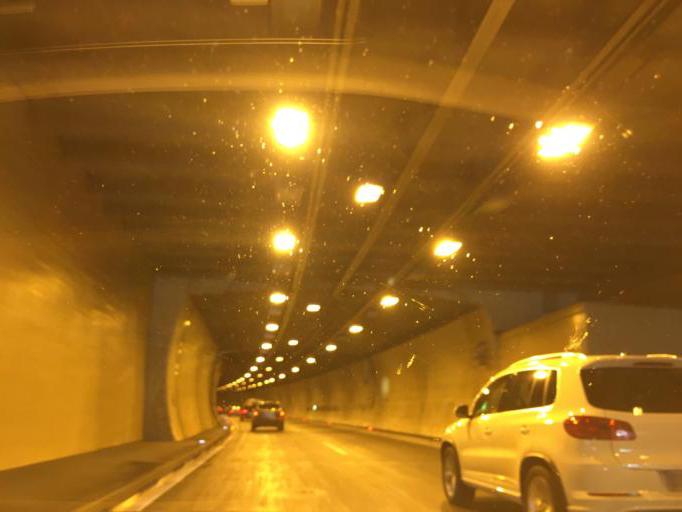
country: AT
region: Salzburg
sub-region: Politischer Bezirk Tamsweg
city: Sankt Michael im Lungau
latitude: 47.0793
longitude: 13.5959
